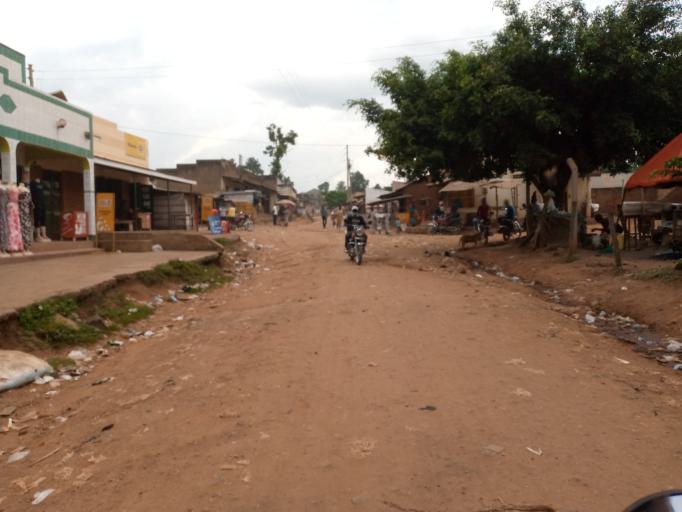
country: UG
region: Eastern Region
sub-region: Mbale District
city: Mbale
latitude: 1.0855
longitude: 34.1665
